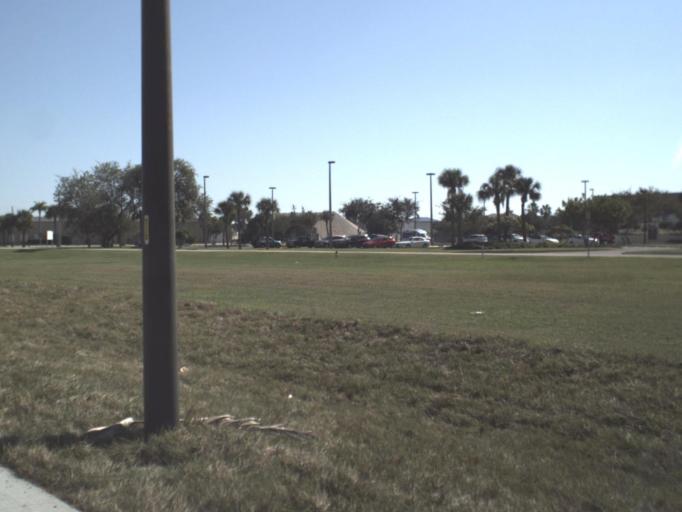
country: US
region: Florida
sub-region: Brevard County
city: Cape Canaveral
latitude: 28.4049
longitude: -80.6130
